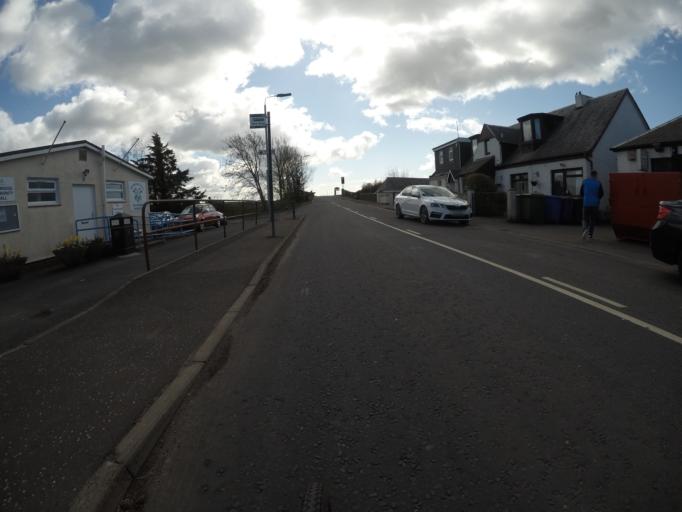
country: GB
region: Scotland
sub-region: North Ayrshire
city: Dreghorn
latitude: 55.5948
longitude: -4.6043
